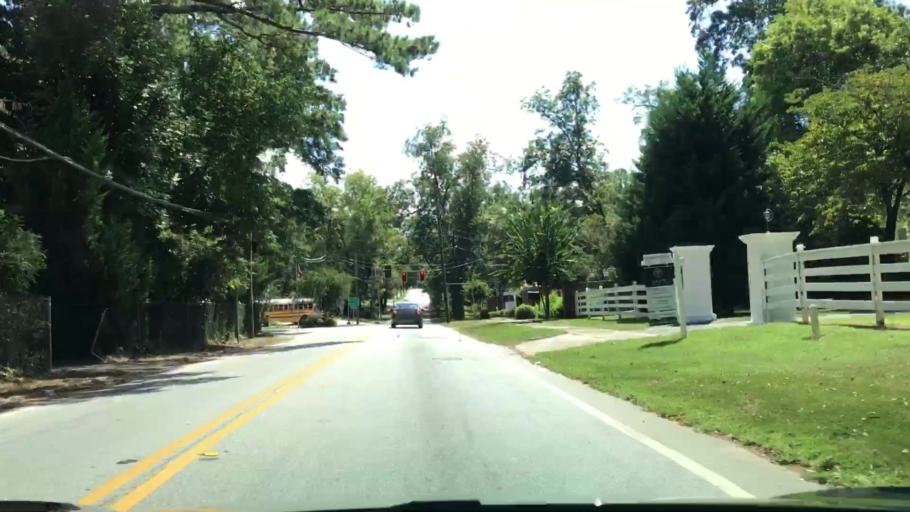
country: US
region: Georgia
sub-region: Greene County
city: Greensboro
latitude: 33.5770
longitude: -83.1880
